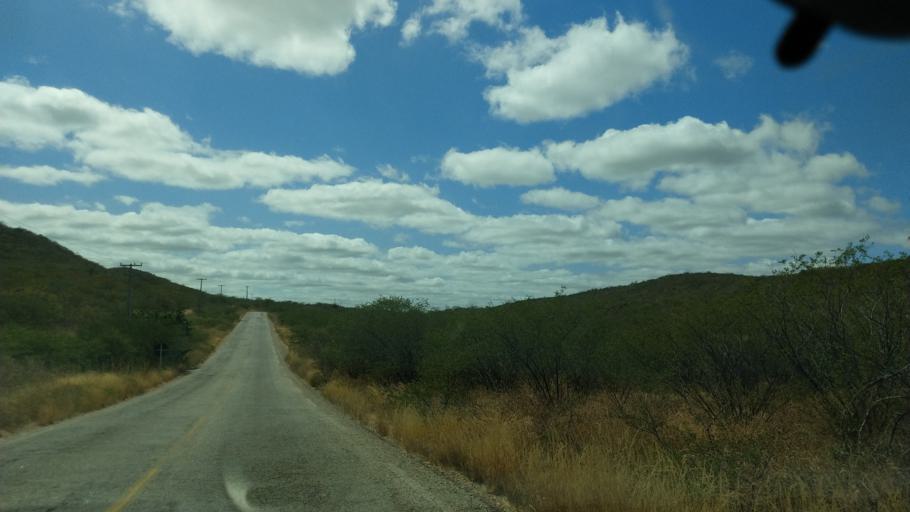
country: BR
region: Rio Grande do Norte
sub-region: Currais Novos
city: Currais Novos
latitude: -6.2630
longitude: -36.5864
